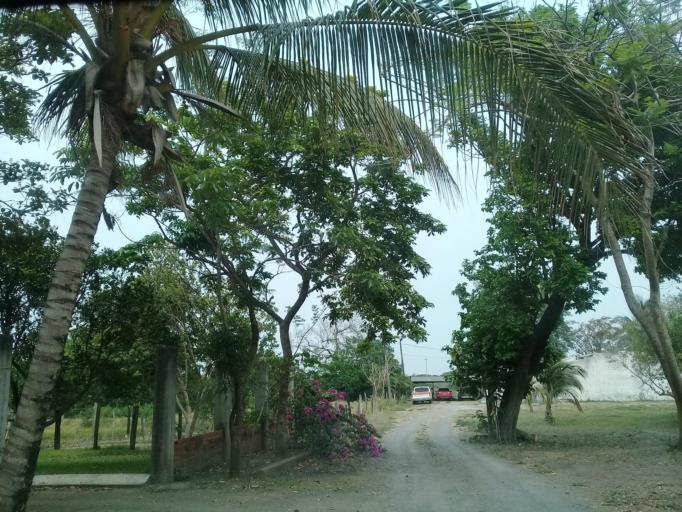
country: MX
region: Veracruz
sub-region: Veracruz
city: Hacienda Sotavento
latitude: 19.1450
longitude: -96.1741
